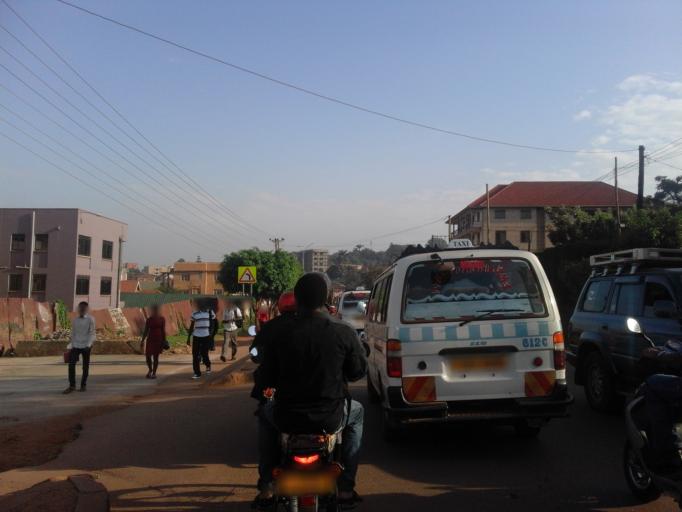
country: UG
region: Central Region
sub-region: Kampala District
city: Kampala
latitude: 0.2951
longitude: 32.6051
